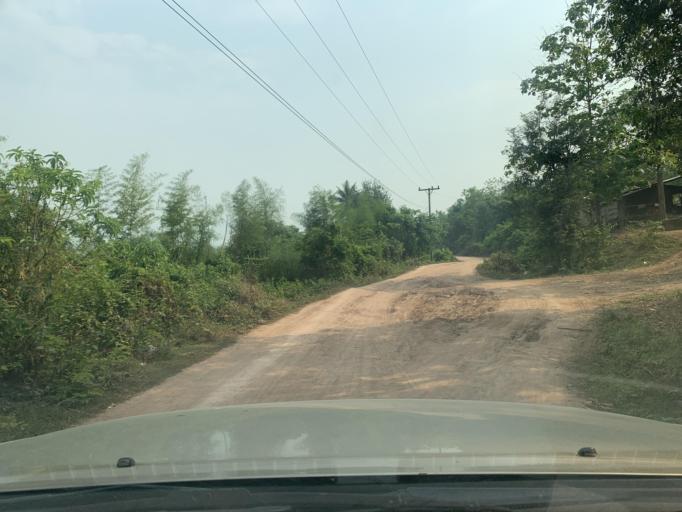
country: LA
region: Louangphabang
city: Louangphabang
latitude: 19.9060
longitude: 102.1306
